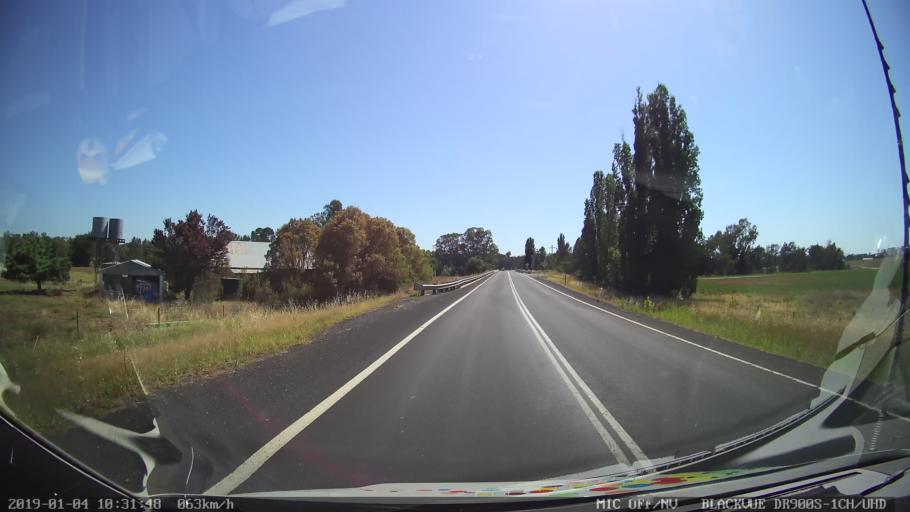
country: AU
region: New South Wales
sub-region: Cabonne
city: Canowindra
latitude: -33.3310
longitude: 148.6336
